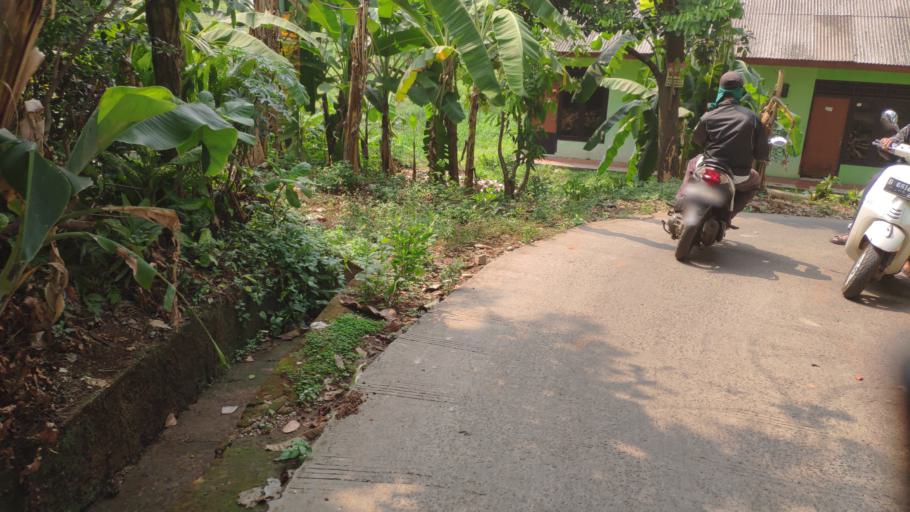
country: ID
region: West Java
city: Depok
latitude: -6.3829
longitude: 106.7966
